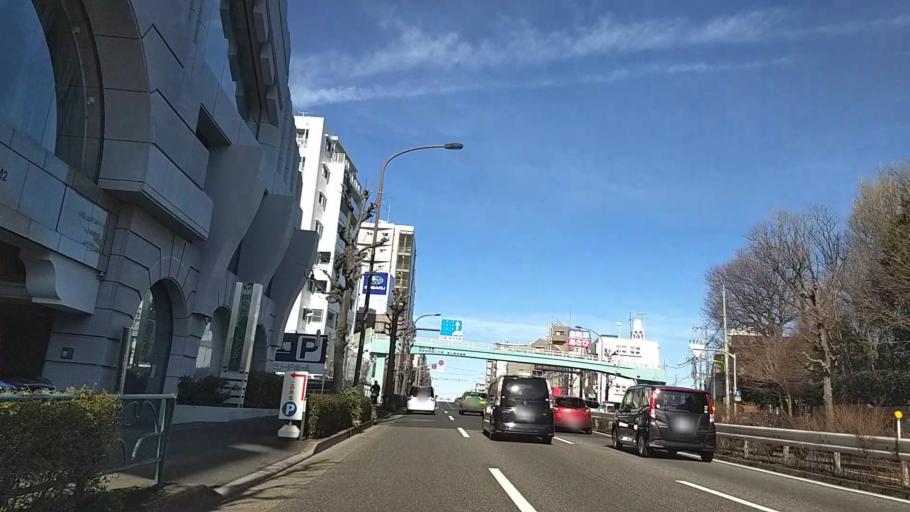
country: JP
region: Tokyo
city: Mitaka-shi
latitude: 35.6415
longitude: 139.6191
